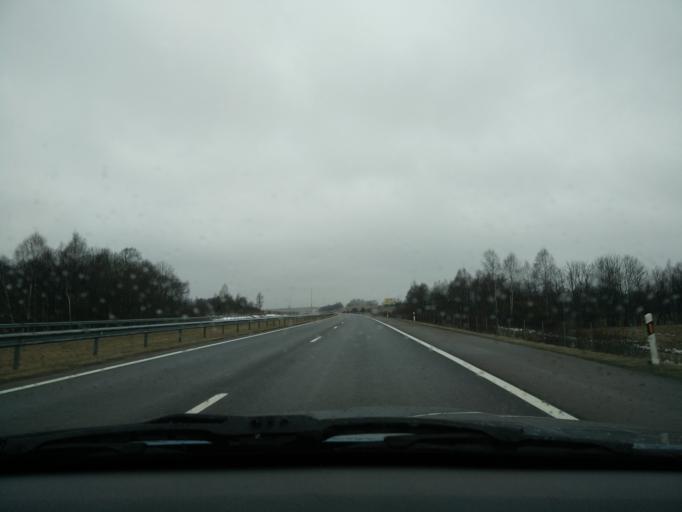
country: LT
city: Silale
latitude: 55.5529
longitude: 22.2598
